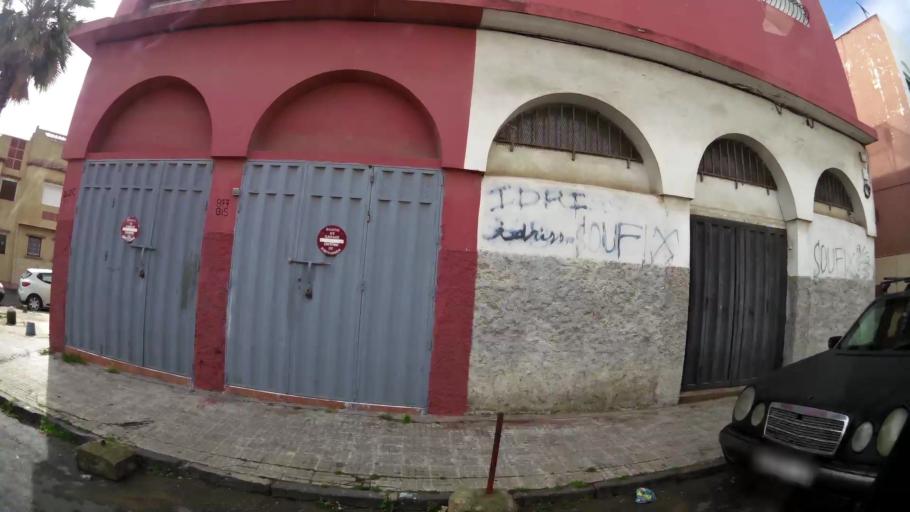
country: MA
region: Grand Casablanca
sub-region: Casablanca
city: Casablanca
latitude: 33.5644
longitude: -7.6698
